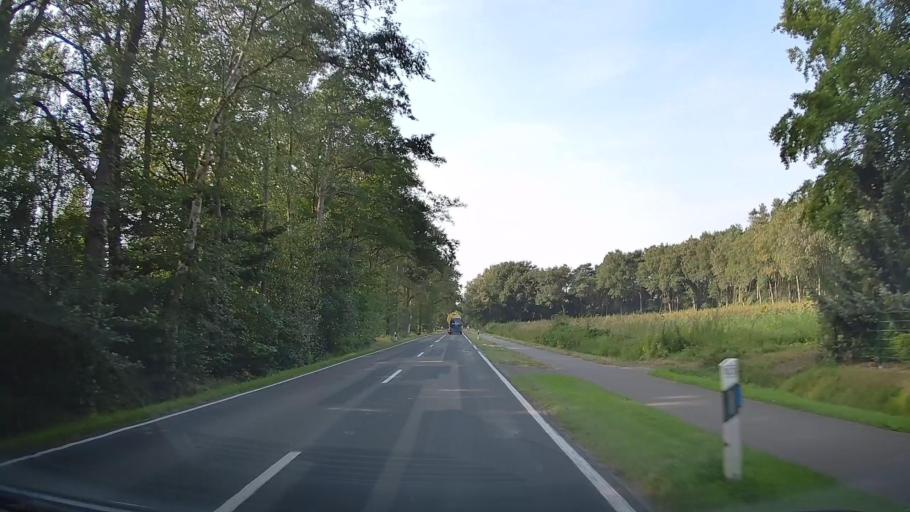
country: DE
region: Lower Saxony
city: Friesoythe
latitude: 53.1118
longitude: 7.8279
